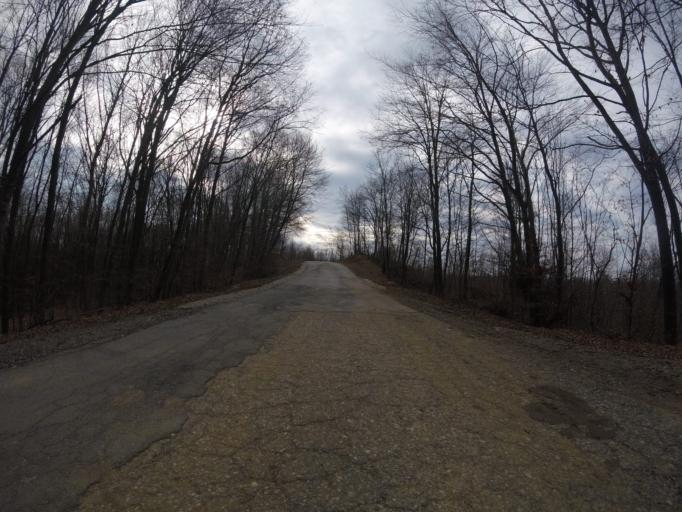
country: HR
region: Zagrebacka
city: Mraclin
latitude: 45.5195
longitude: 16.0492
